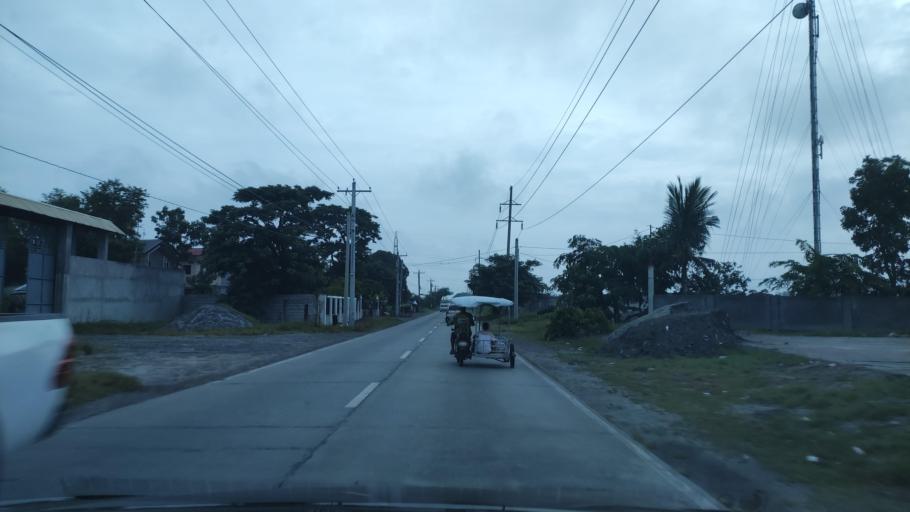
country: PH
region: Central Luzon
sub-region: Province of Pampanga
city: Laug
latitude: 15.0503
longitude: 120.7520
